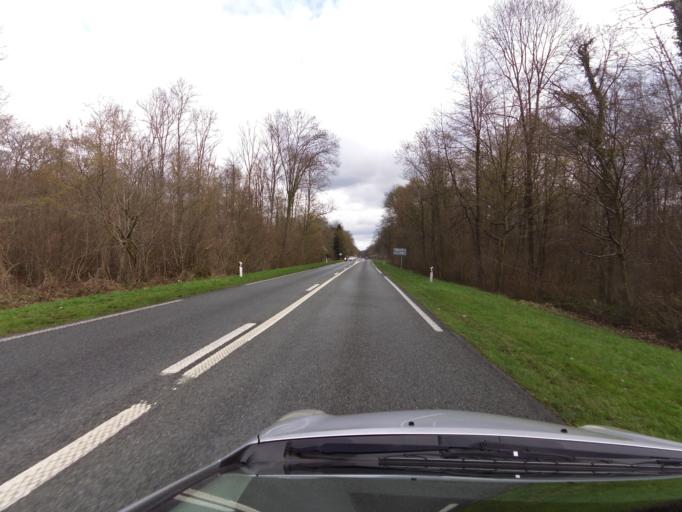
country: FR
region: Picardie
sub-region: Departement de l'Oise
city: Pont-Sainte-Maxence
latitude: 49.2813
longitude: 2.5980
